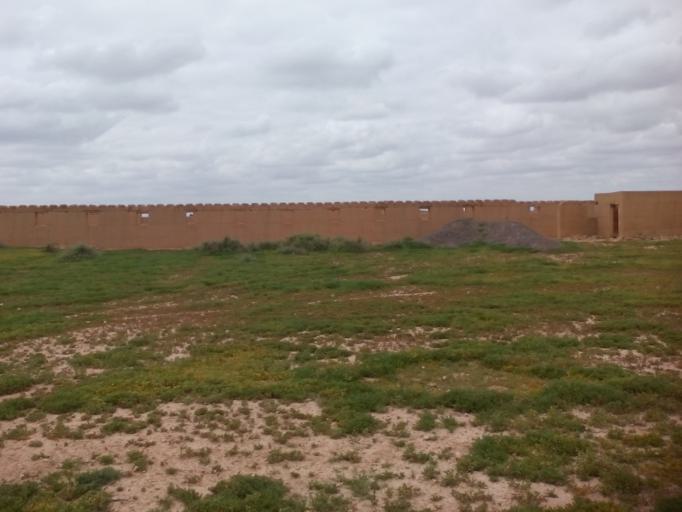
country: MA
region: Marrakech-Tensift-Al Haouz
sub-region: Marrakech
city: Marrakesh
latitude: 31.6450
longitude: -8.3029
